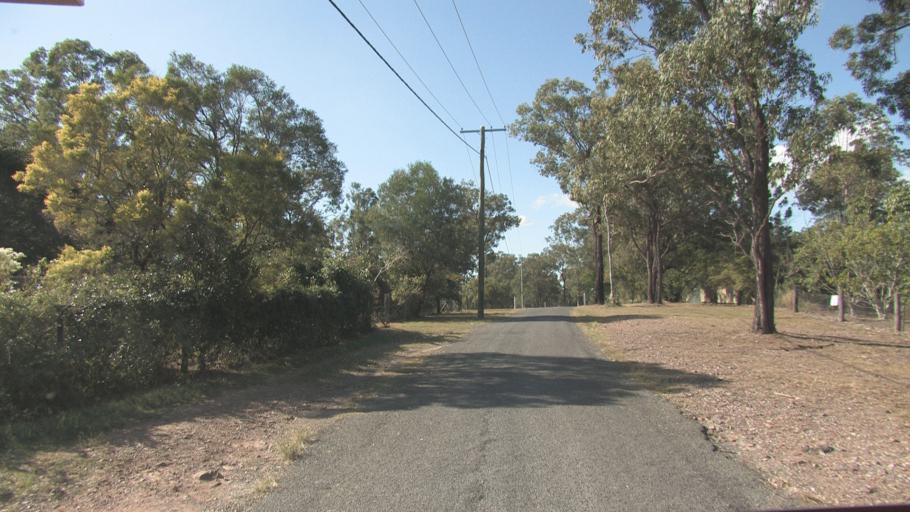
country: AU
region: Queensland
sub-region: Logan
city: Windaroo
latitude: -27.7411
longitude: 153.1558
